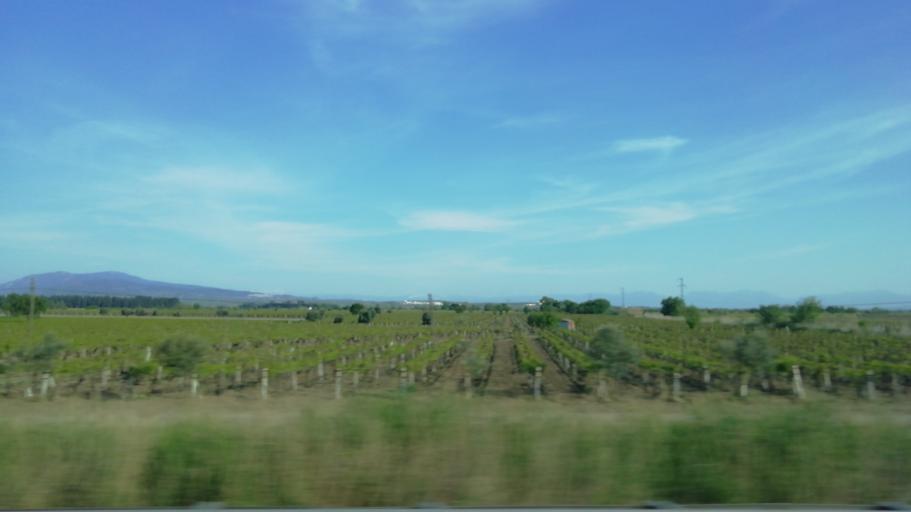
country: TR
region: Manisa
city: Saruhanli
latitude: 38.7248
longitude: 27.5702
